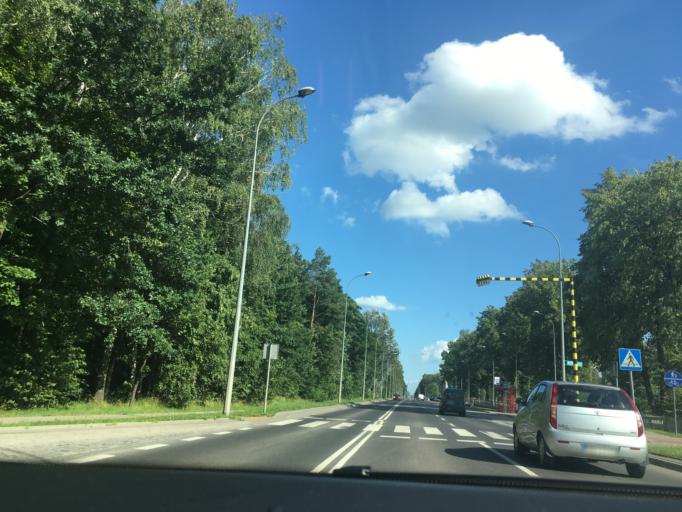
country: PL
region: Podlasie
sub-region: Bialystok
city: Bialystok
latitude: 53.1068
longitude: 23.2145
